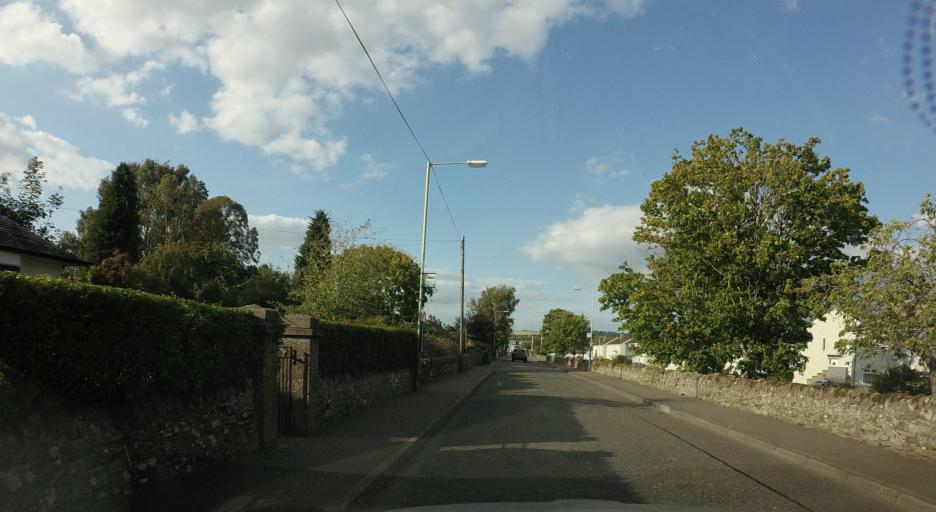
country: GB
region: Scotland
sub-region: Angus
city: Muirhead
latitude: 56.4582
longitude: -3.0624
